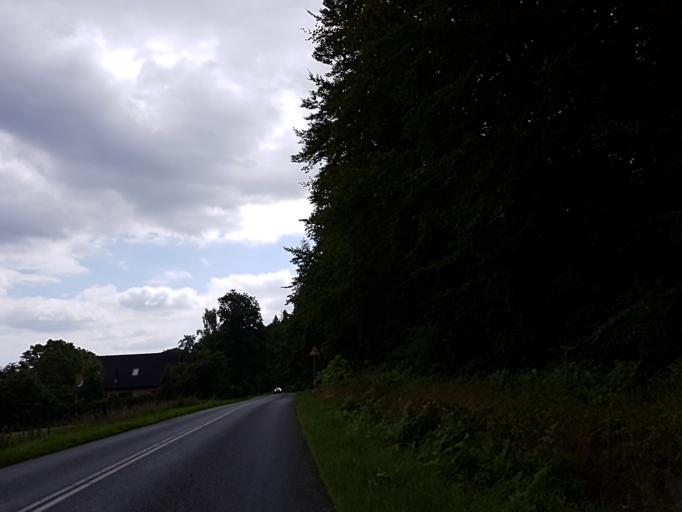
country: DK
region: Capital Region
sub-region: Fureso Kommune
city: Farum
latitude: 55.8105
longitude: 12.3220
